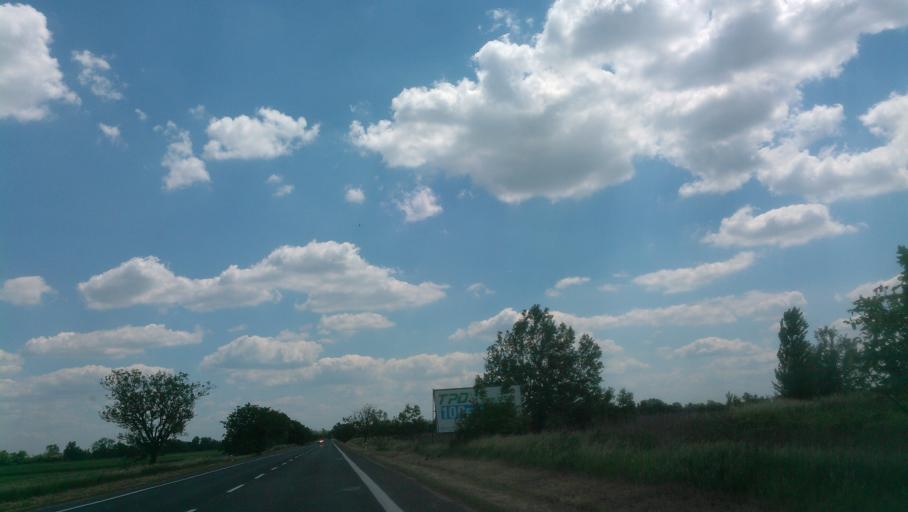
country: SK
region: Trnavsky
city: Samorin
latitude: 48.0509
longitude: 17.2904
